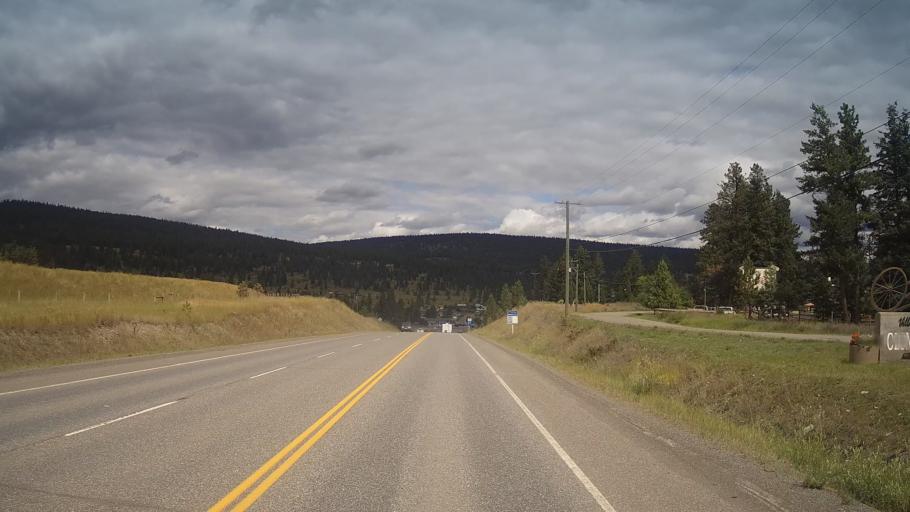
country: CA
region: British Columbia
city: Cache Creek
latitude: 51.0822
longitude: -121.5910
